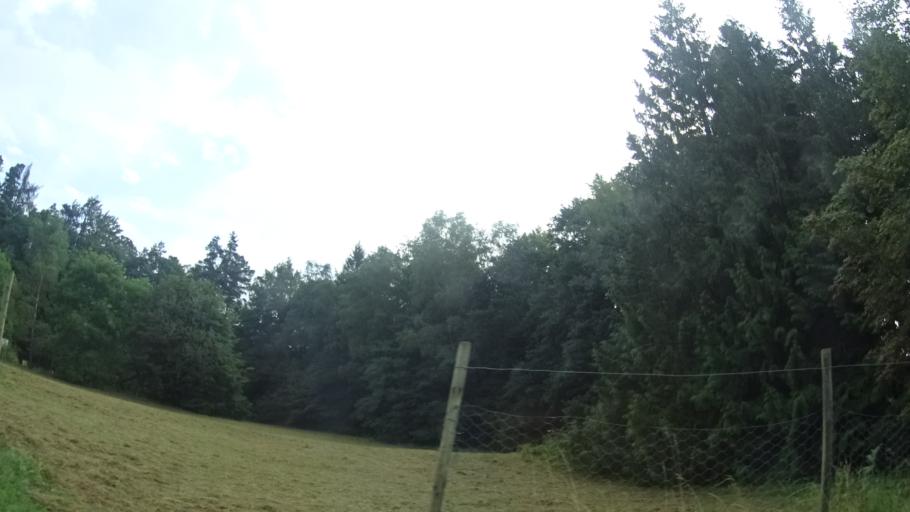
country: DE
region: Baden-Wuerttemberg
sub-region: Karlsruhe Region
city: Dobel
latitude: 48.7940
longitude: 8.5037
